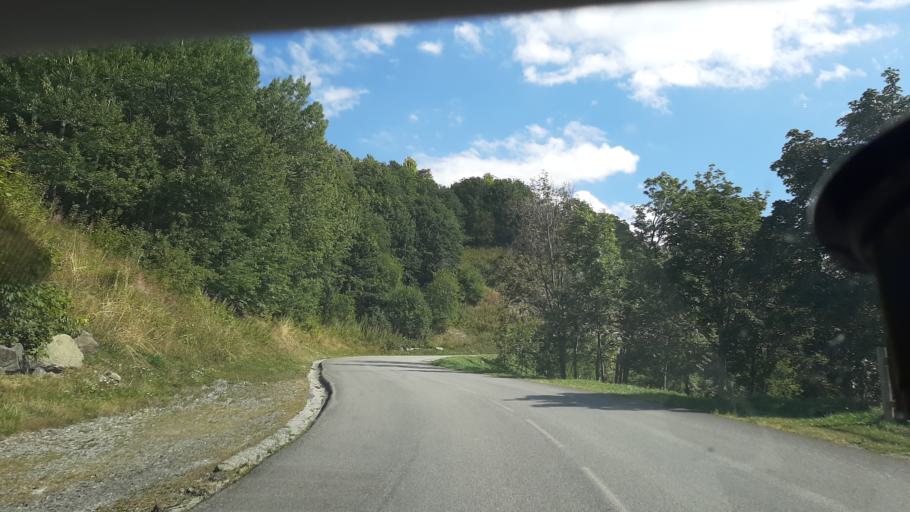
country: FR
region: Rhone-Alpes
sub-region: Departement de la Savoie
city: Saint-Michel-de-Maurienne
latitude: 45.1801
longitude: 6.4861
